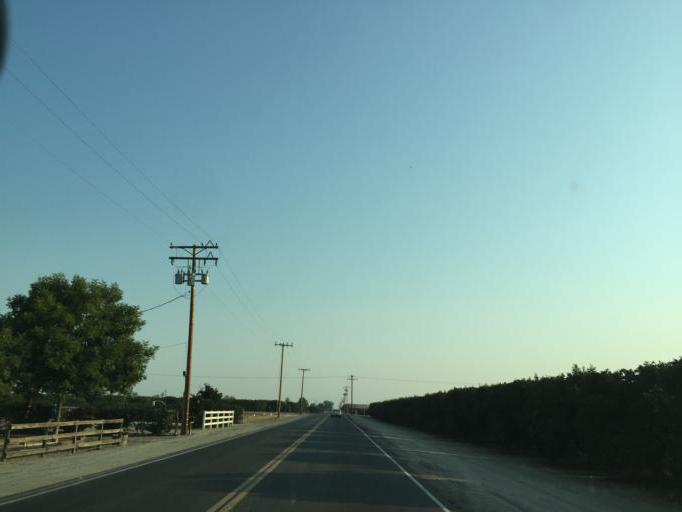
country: US
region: California
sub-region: Tulare County
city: Ivanhoe
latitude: 36.4268
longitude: -119.2779
